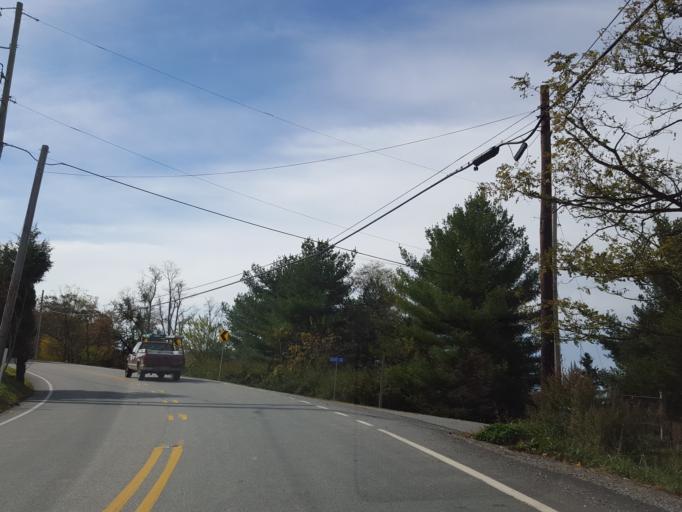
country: US
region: Pennsylvania
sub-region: York County
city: Wrightsville
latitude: 39.9944
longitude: -76.5559
